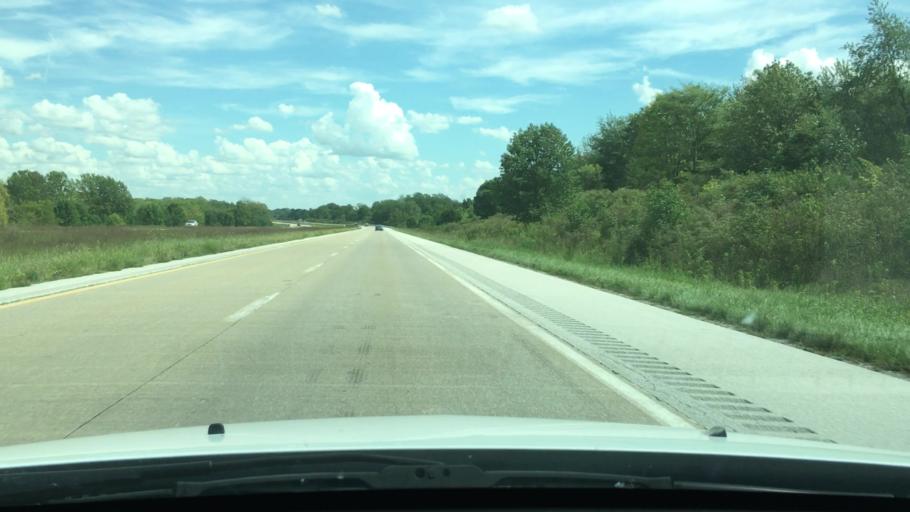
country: US
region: Illinois
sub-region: Scott County
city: Winchester
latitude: 39.6819
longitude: -90.5260
